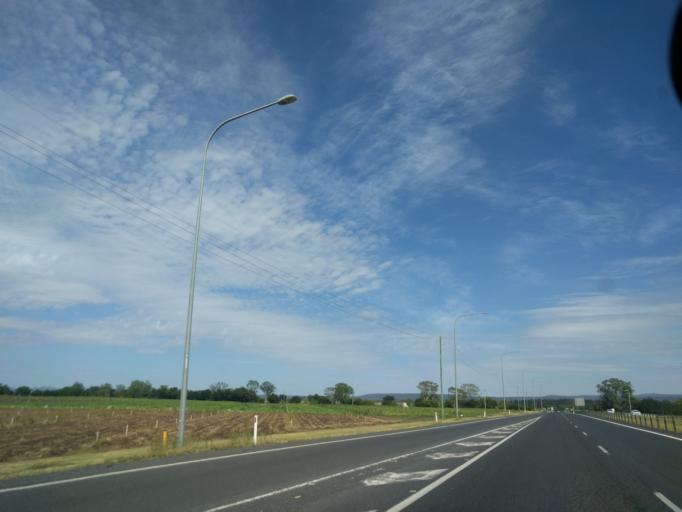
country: AU
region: Queensland
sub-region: Lockyer Valley
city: Gatton
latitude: -27.5478
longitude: 152.3145
